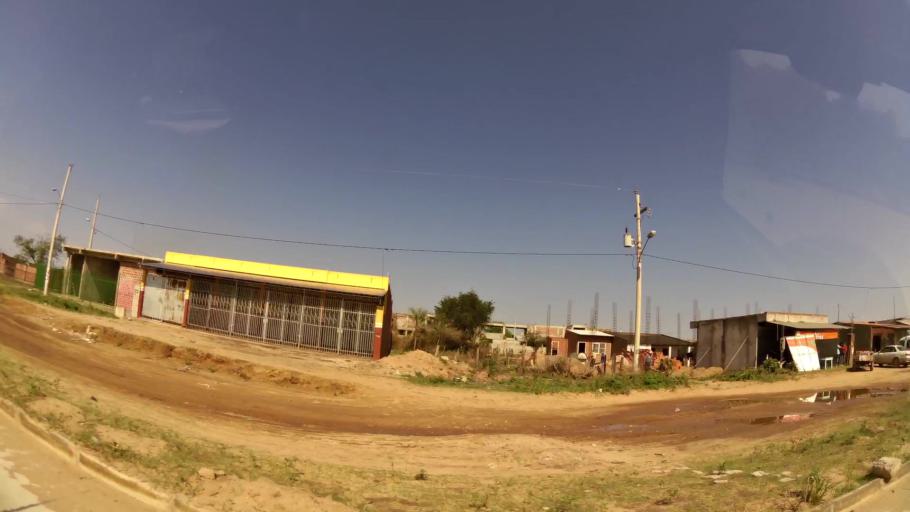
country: BO
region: Santa Cruz
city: Cotoca
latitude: -17.7163
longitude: -63.0705
